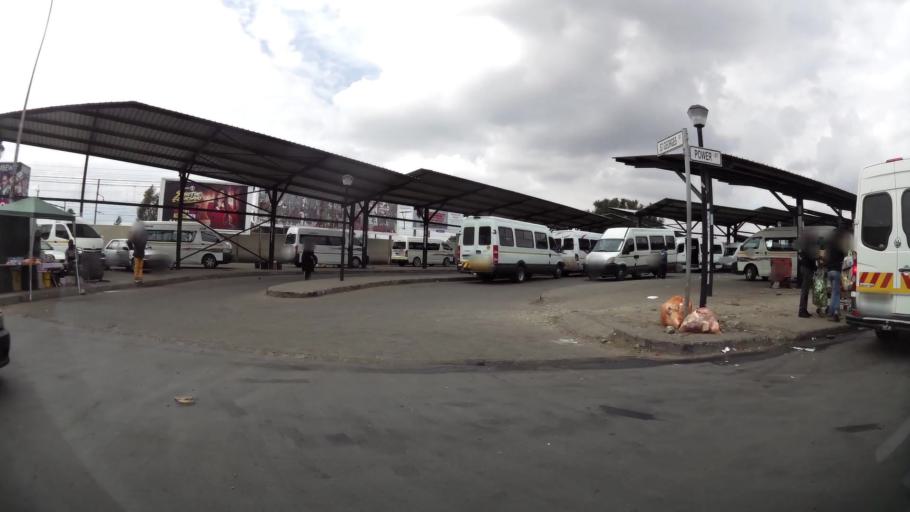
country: ZA
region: Orange Free State
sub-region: Mangaung Metropolitan Municipality
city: Bloemfontein
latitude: -29.1222
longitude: 26.2260
